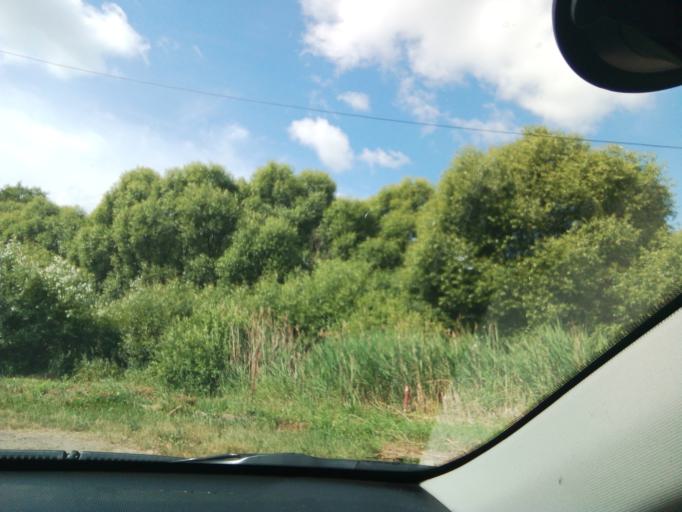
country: RU
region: Tambov
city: Goreloye
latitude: 53.0523
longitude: 41.4788
